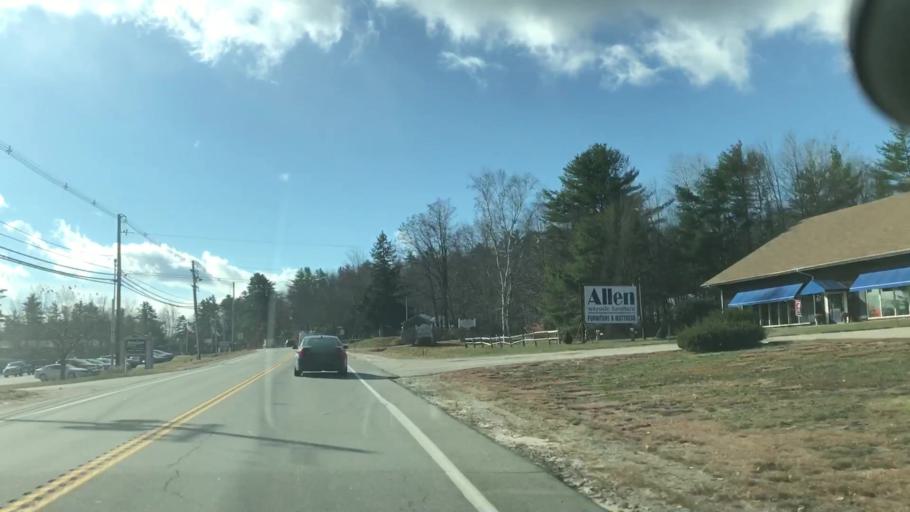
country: US
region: New Hampshire
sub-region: Carroll County
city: Wolfeboro
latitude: 43.6176
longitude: -71.1734
